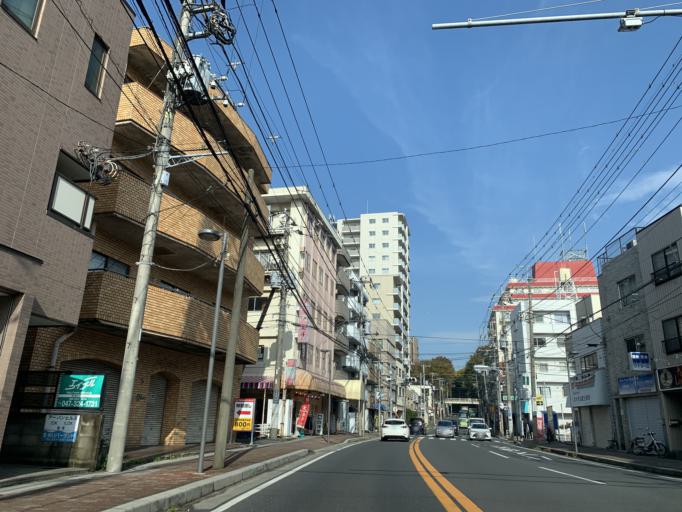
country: JP
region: Chiba
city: Matsudo
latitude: 35.7390
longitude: 139.9030
